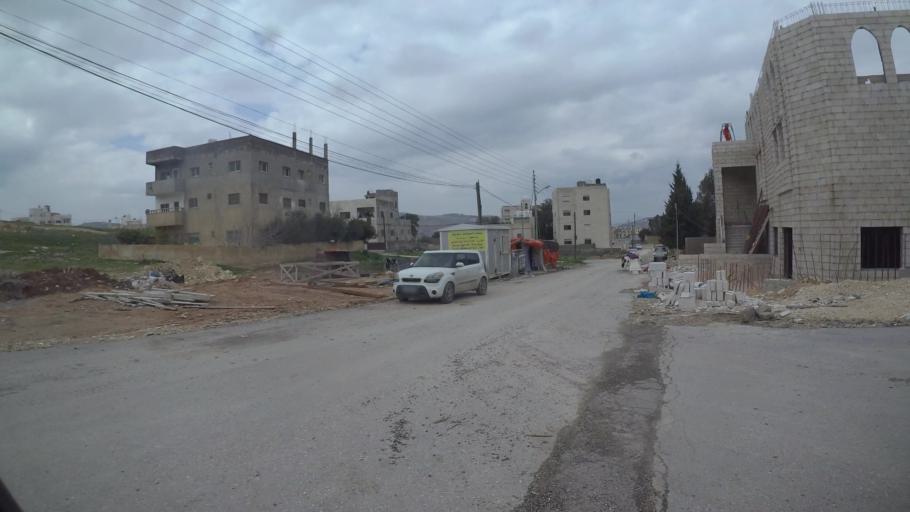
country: JO
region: Amman
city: Al Jubayhah
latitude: 32.0513
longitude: 35.8415
